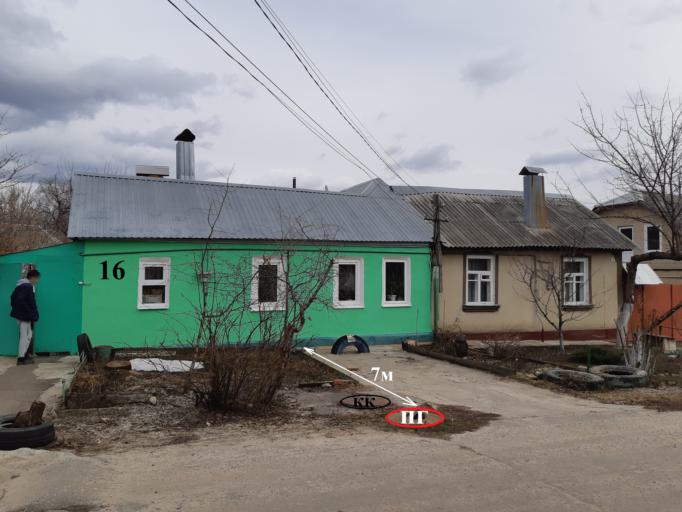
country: RU
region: Voronezj
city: Voronezh
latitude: 51.6961
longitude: 39.1631
